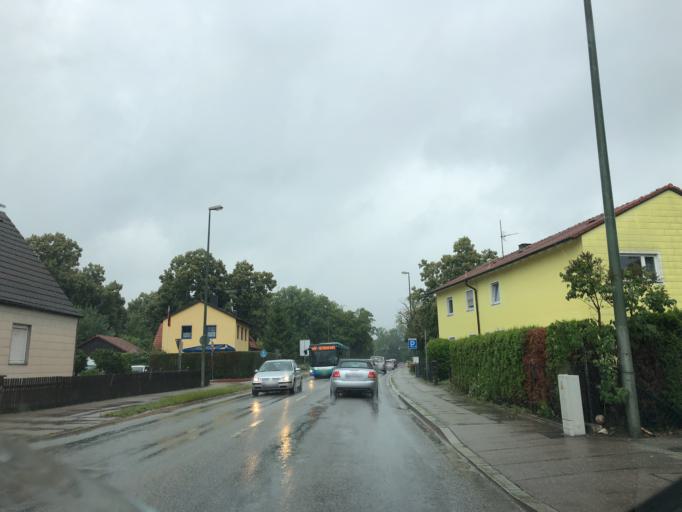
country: DE
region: Bavaria
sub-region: Upper Bavaria
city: Erding
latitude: 48.3129
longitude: 11.9075
